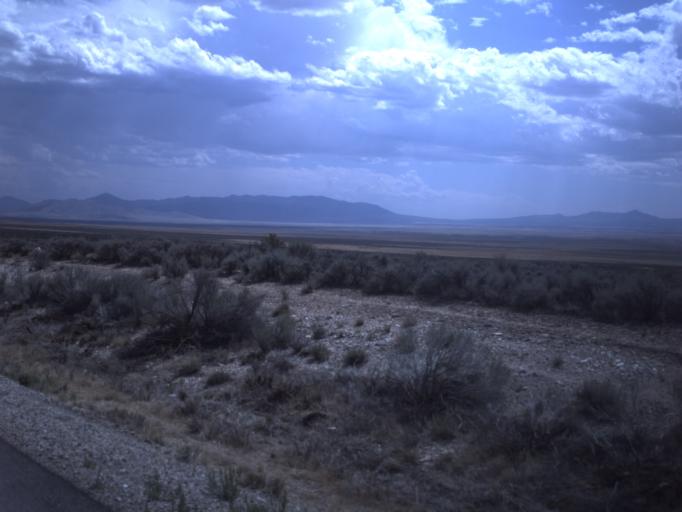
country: US
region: Utah
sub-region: Tooele County
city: Tooele
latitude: 40.2857
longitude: -112.2644
